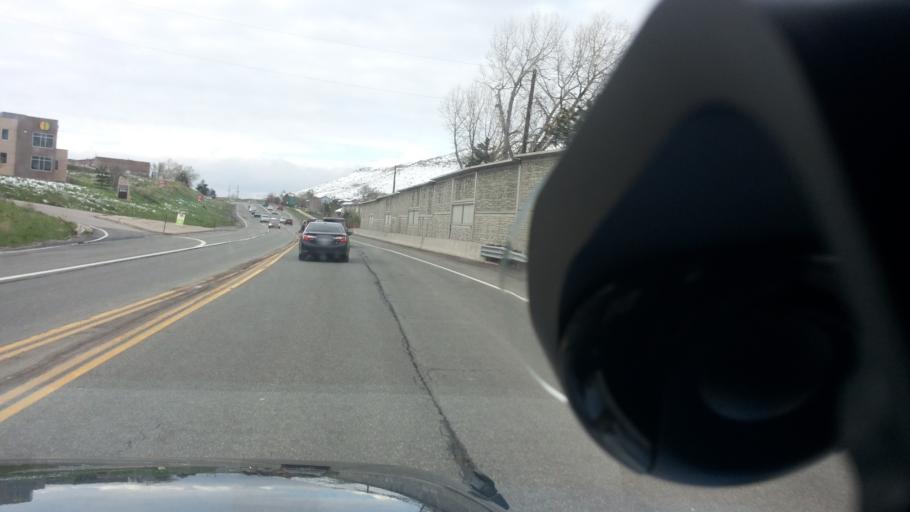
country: US
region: Colorado
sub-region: Jefferson County
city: Golden
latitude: 39.7750
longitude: -105.2342
